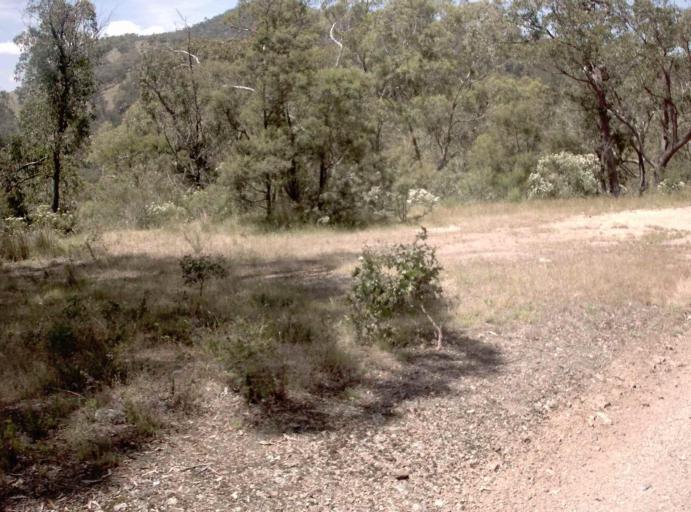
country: AU
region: Victoria
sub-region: East Gippsland
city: Bairnsdale
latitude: -37.4238
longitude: 147.8318
